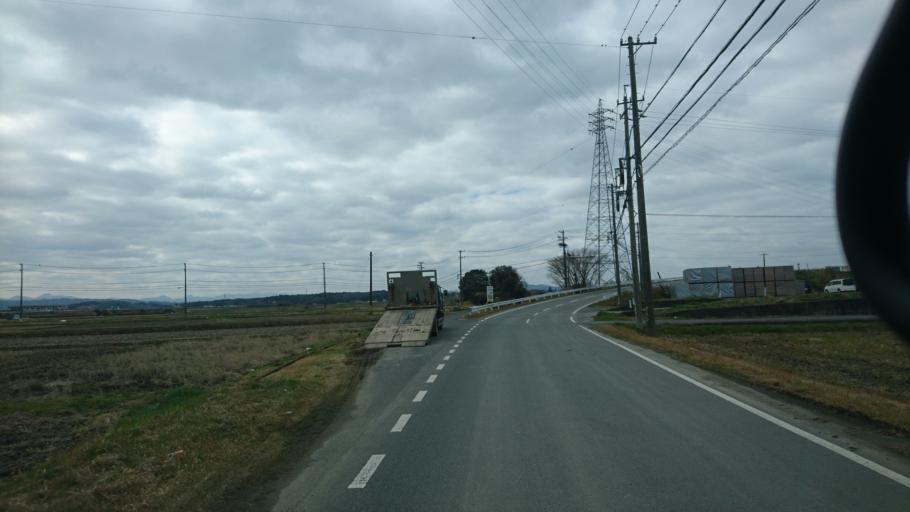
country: JP
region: Mie
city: Ueno-ebisumachi
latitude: 34.7524
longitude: 136.1195
